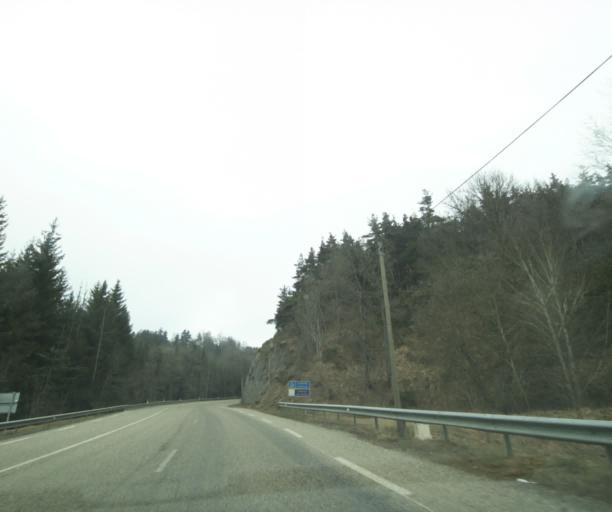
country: FR
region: Languedoc-Roussillon
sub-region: Departement de la Lozere
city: Langogne
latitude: 44.7431
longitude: 3.8629
